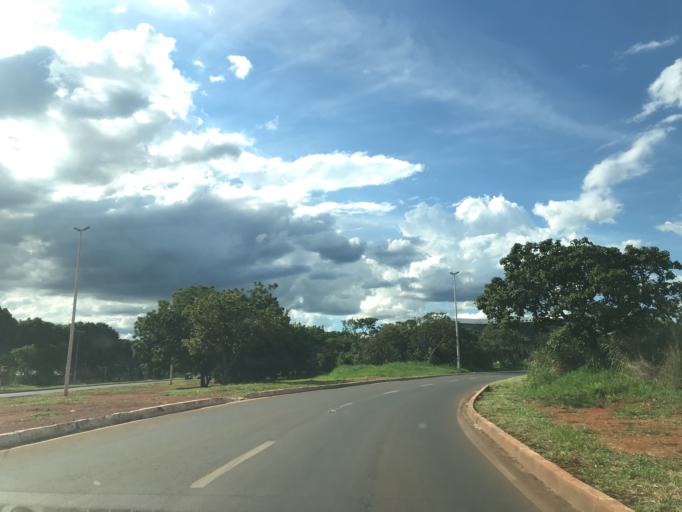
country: BR
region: Federal District
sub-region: Brasilia
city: Brasilia
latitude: -15.8164
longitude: -47.8674
